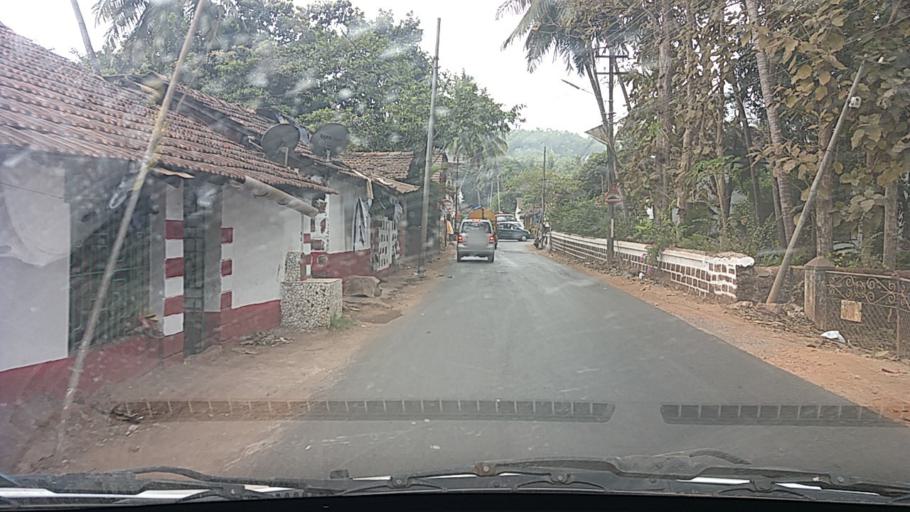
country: IN
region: Goa
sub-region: North Goa
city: Saligao
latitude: 15.5413
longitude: 73.7896
